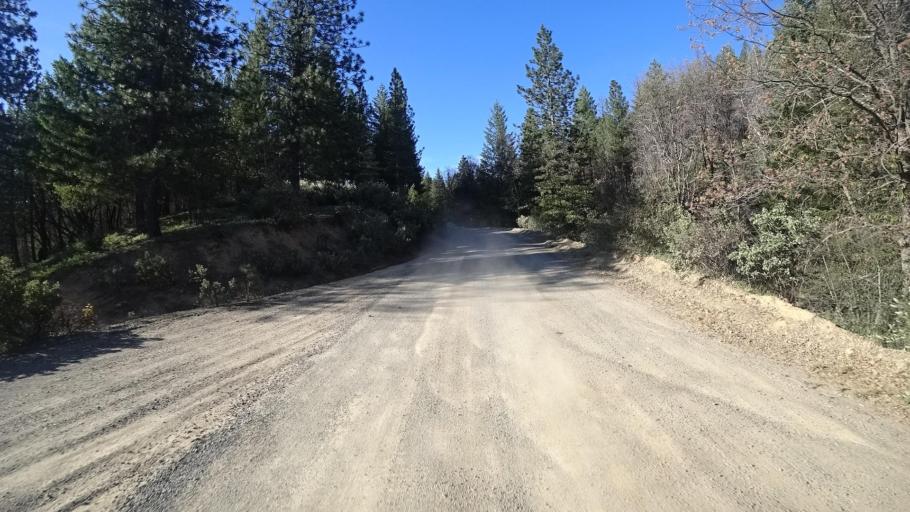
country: US
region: California
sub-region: Lake County
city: Upper Lake
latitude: 39.3197
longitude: -122.9449
